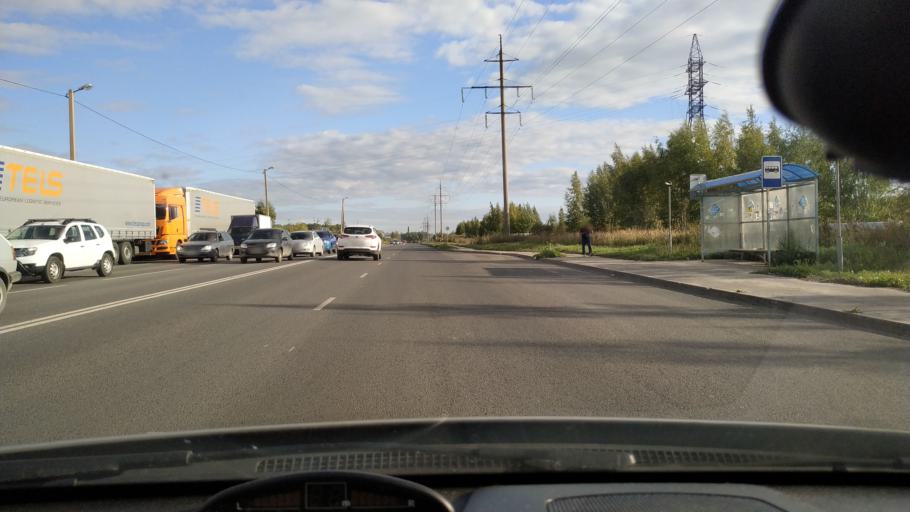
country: RU
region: Rjazan
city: Ryazan'
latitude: 54.5899
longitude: 39.8143
